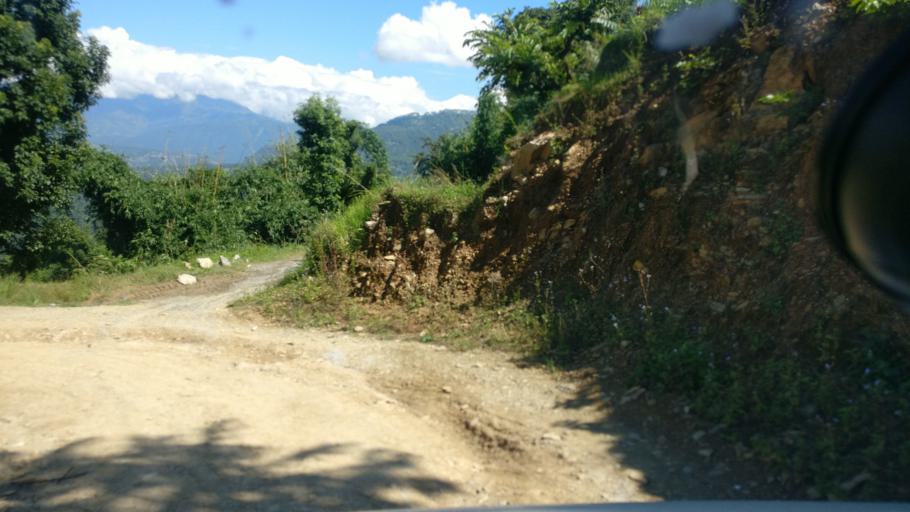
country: NP
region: Western Region
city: Baglung
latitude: 28.1426
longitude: 83.6466
